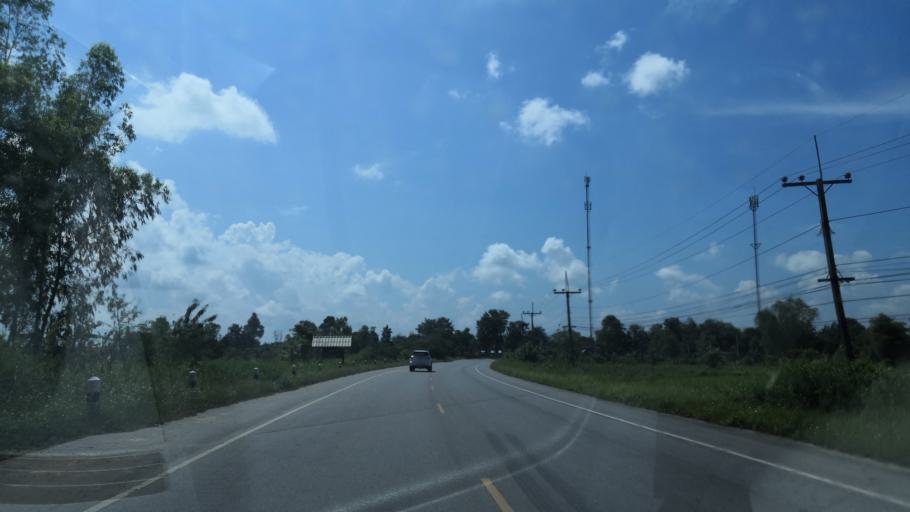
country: TH
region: Chiang Rai
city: Wiang Chiang Rung
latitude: 19.9674
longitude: 100.0116
